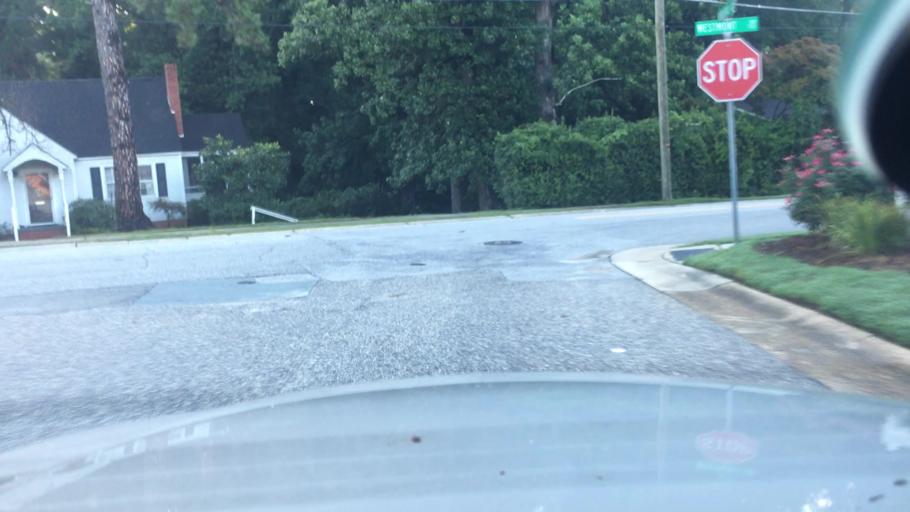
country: US
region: North Carolina
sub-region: Cumberland County
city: Fayetteville
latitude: 35.0668
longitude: -78.9051
